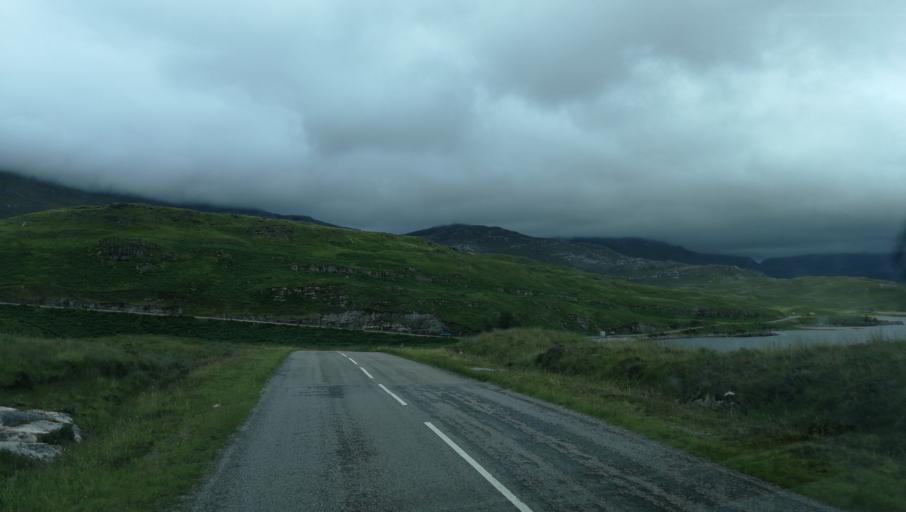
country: GB
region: Scotland
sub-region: Highland
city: Ullapool
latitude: 58.1737
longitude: -5.0077
